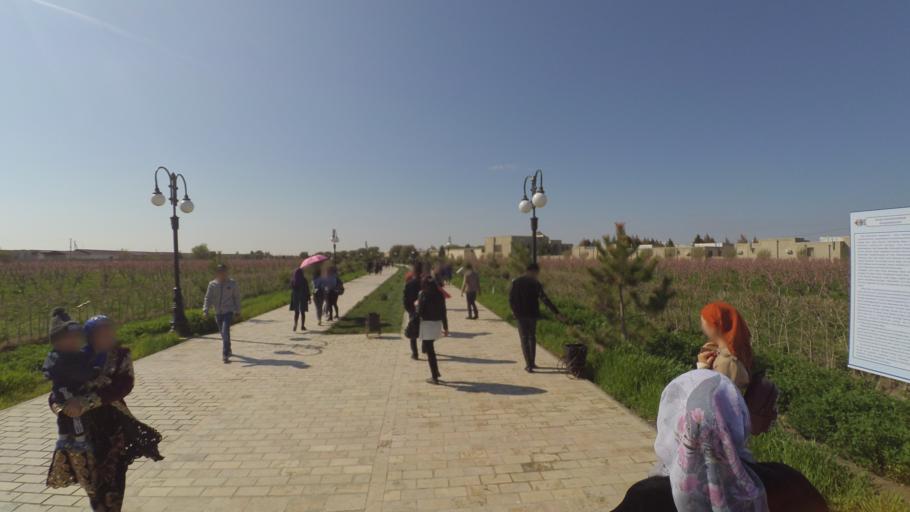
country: UZ
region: Bukhara
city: Kogon
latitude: 39.8036
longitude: 64.5393
